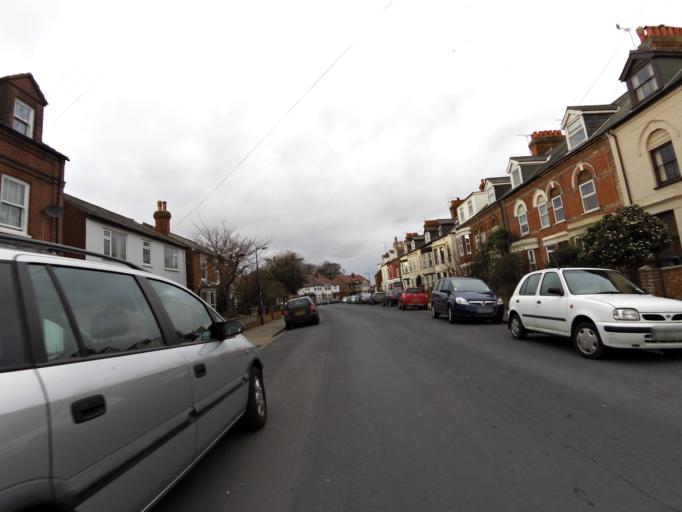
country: GB
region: England
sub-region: Suffolk
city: Felixstowe
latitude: 51.9646
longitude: 1.3570
